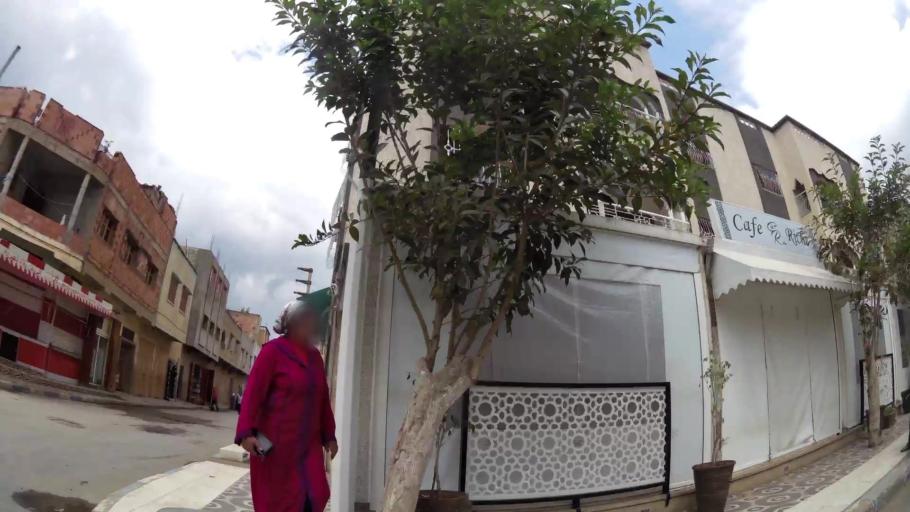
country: MA
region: Rabat-Sale-Zemmour-Zaer
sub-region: Khemisset
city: Tiflet
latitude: 33.8912
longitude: -6.3212
